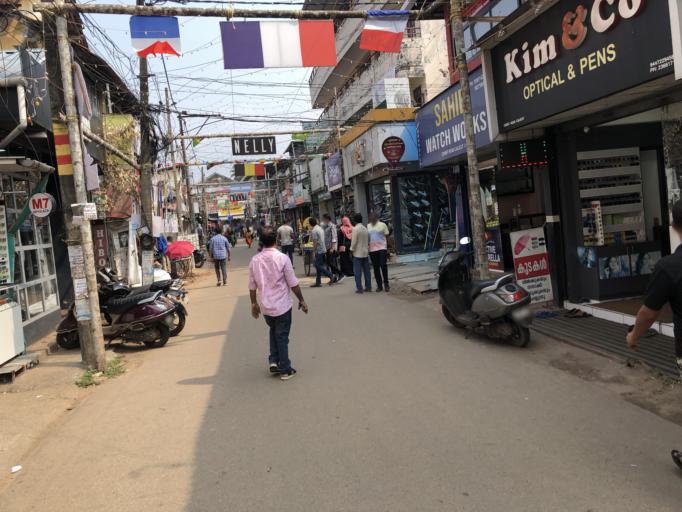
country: IN
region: Kerala
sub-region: Kozhikode
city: Kozhikode
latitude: 11.2515
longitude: 75.7803
